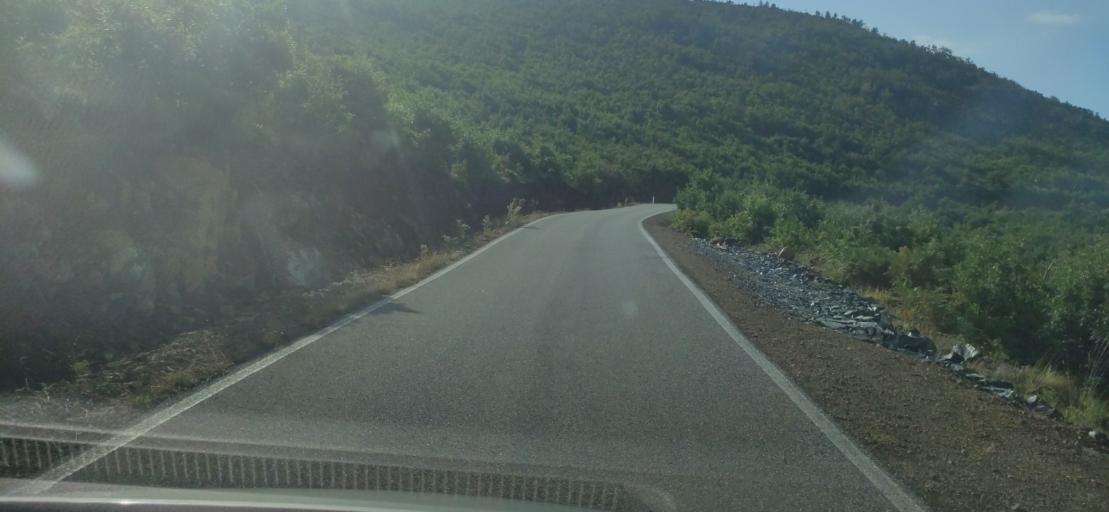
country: AL
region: Shkoder
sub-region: Rrethi i Pukes
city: Iballe
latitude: 42.1710
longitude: 20.0020
